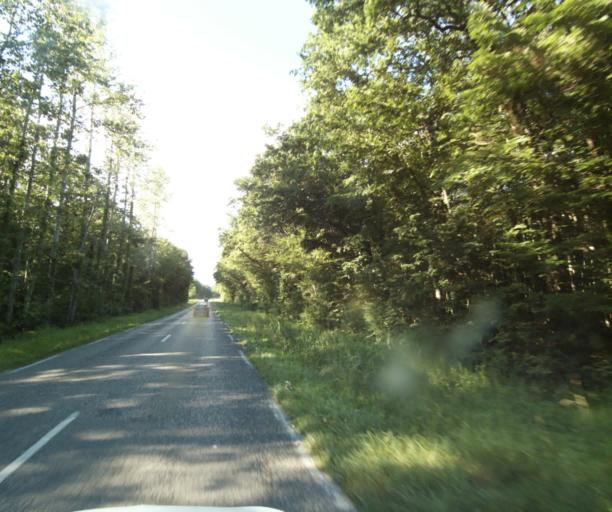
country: FR
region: Rhone-Alpes
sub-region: Departement de la Haute-Savoie
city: Messery
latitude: 46.3331
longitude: 6.2920
